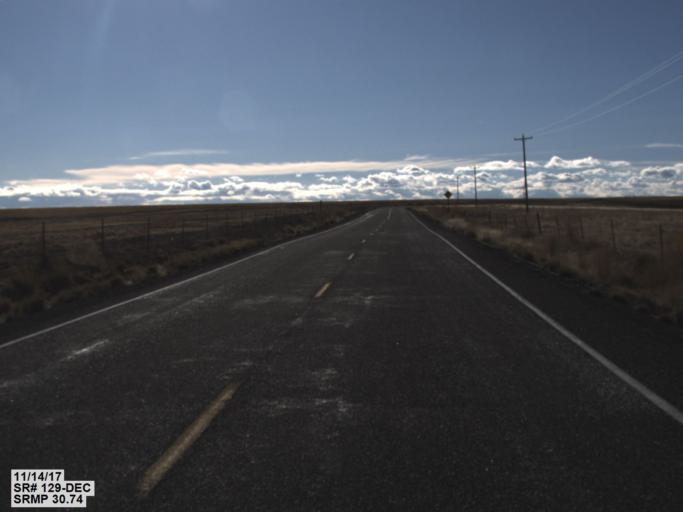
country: US
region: Washington
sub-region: Asotin County
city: Asotin
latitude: 46.3017
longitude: -117.0435
